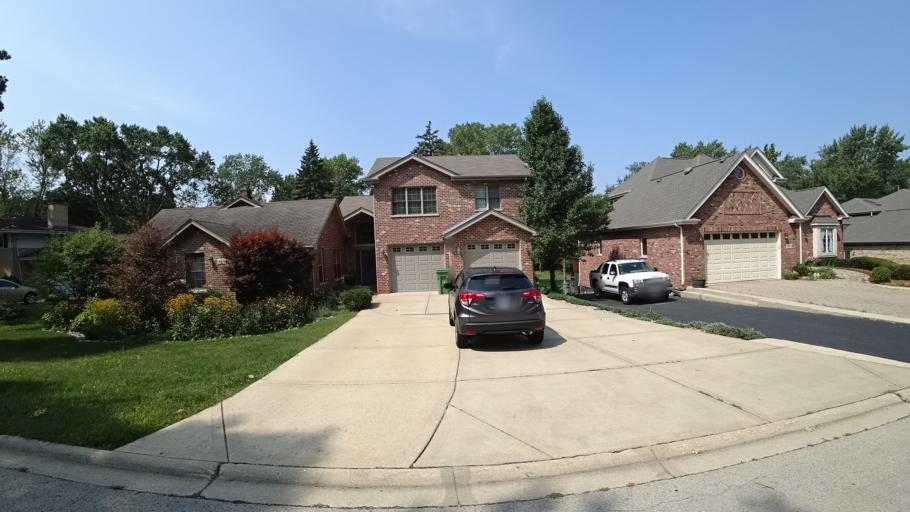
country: US
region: Illinois
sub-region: Cook County
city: Orland Park
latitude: 41.6240
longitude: -87.8657
